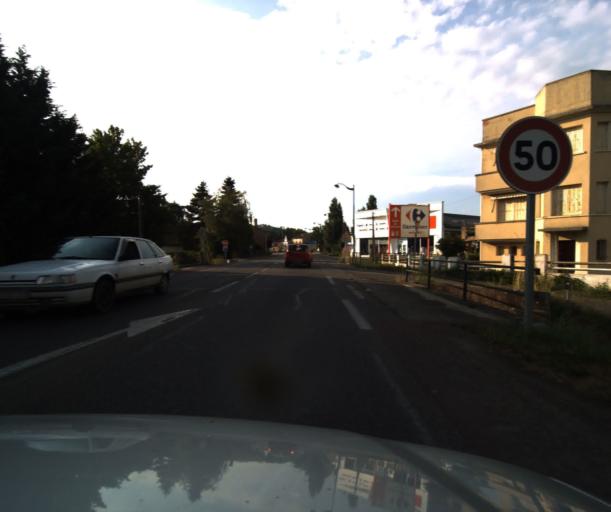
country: FR
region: Midi-Pyrenees
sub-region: Departement du Tarn-et-Garonne
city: Moissac
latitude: 44.0937
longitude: 1.0865
